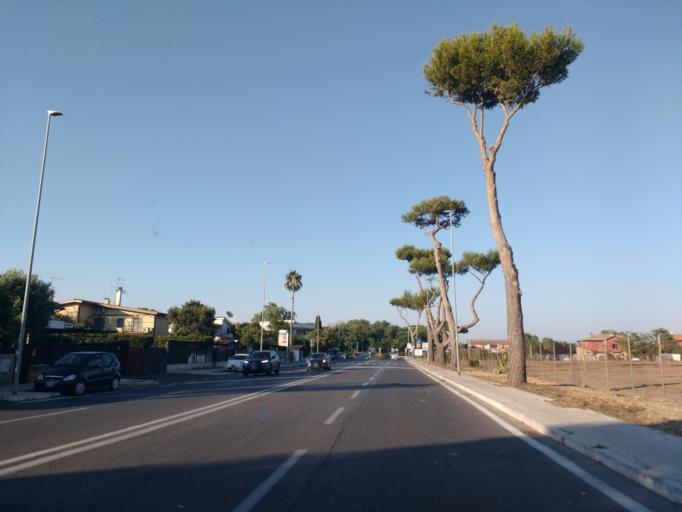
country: IT
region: Latium
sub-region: Citta metropolitana di Roma Capitale
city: Fregene
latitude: 41.8614
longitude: 12.2086
